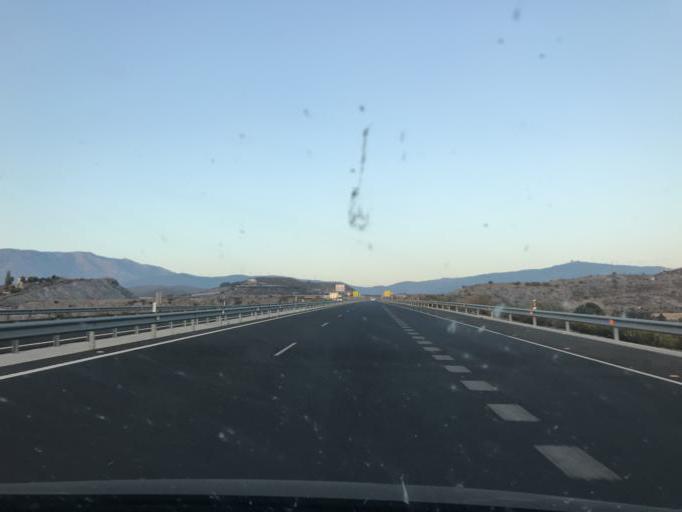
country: ES
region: Andalusia
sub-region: Provincia de Granada
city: Motril
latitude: 36.7371
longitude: -3.4911
